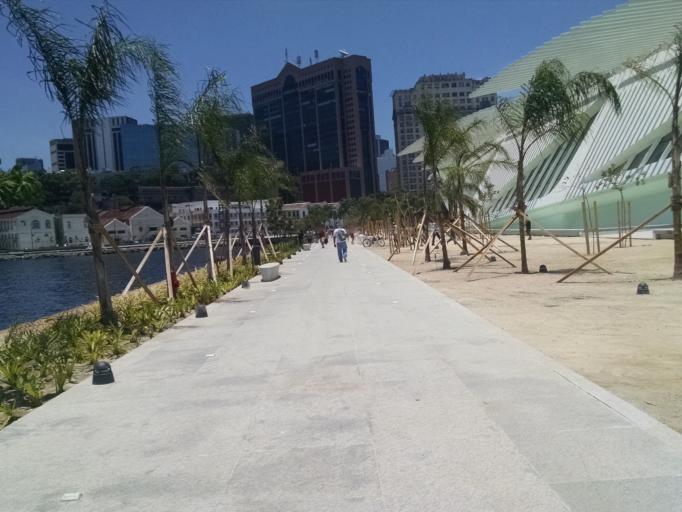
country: BR
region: Rio de Janeiro
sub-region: Rio De Janeiro
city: Rio de Janeiro
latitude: -22.8937
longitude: -43.1789
